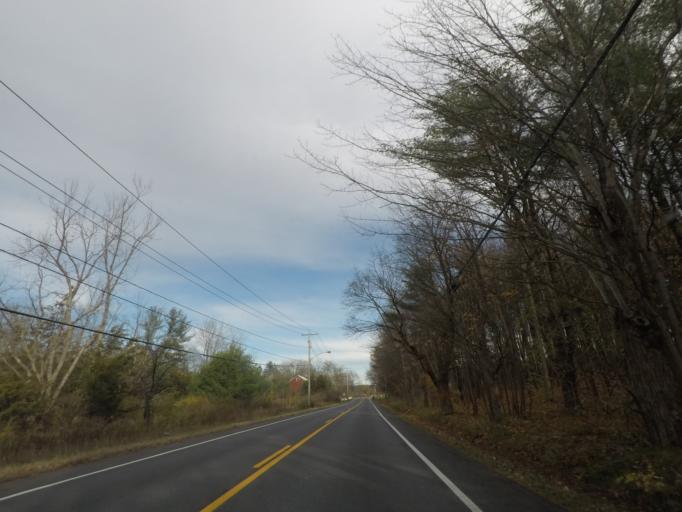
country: US
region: New York
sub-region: Albany County
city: Voorheesville
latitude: 42.6472
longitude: -73.9439
